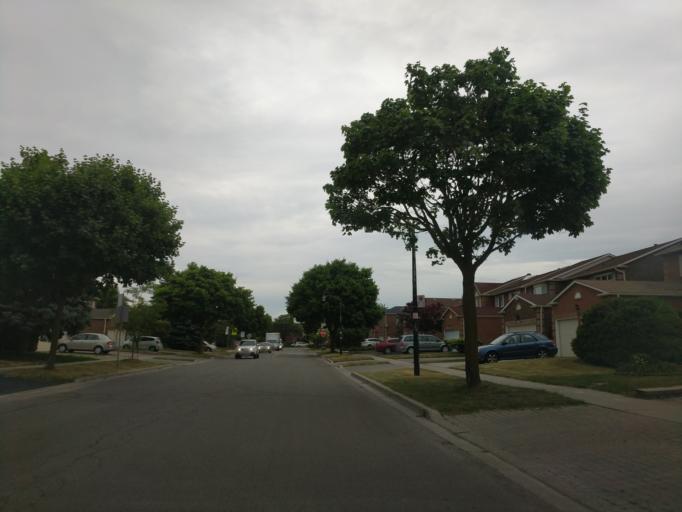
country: CA
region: Ontario
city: Markham
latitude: 43.8189
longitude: -79.3071
